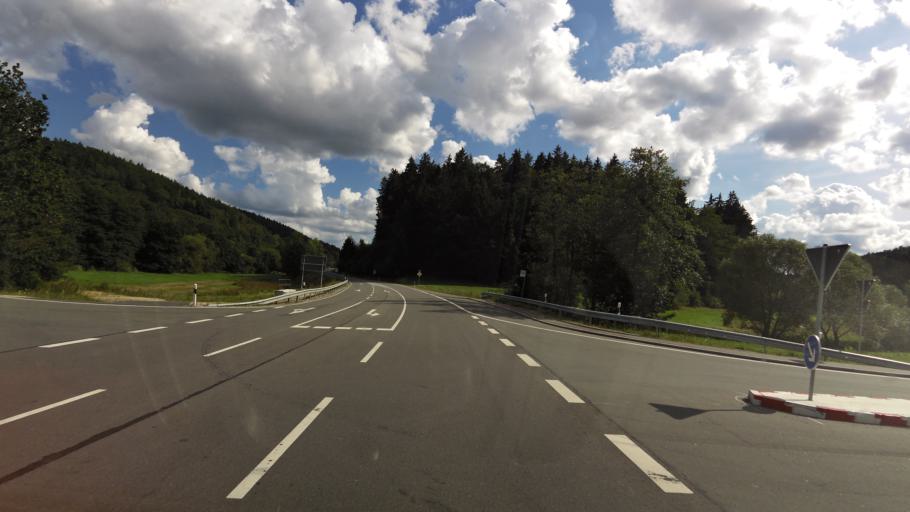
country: DE
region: Bavaria
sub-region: Upper Palatinate
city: Traitsching
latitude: 49.1395
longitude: 12.6507
